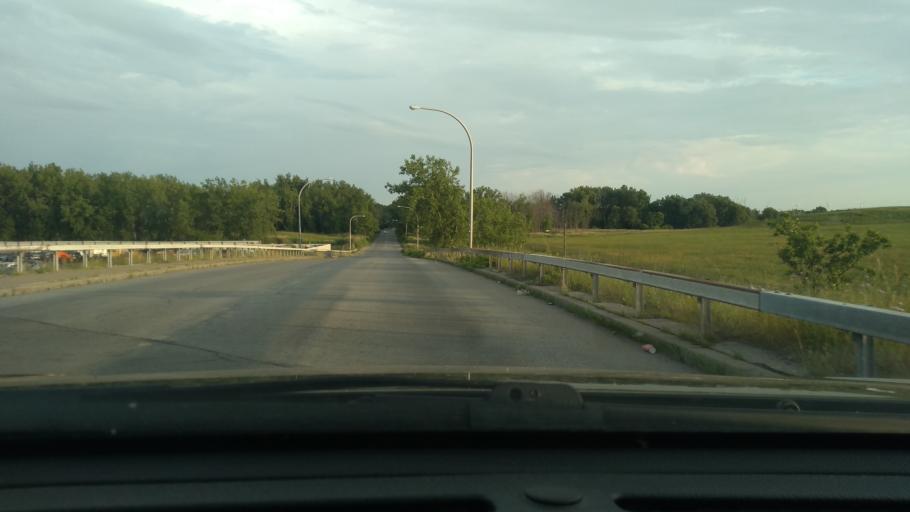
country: US
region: New York
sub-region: Erie County
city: Lackawanna
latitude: 42.8366
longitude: -78.8325
